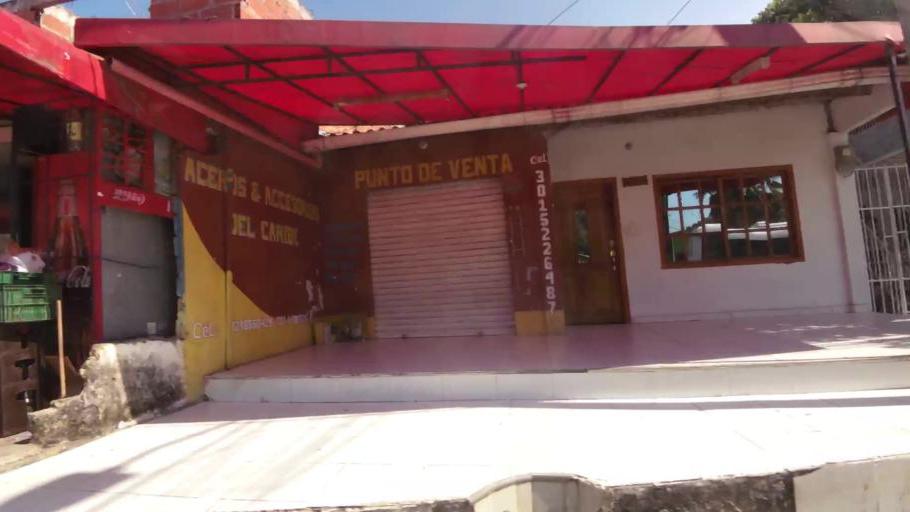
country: CO
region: Bolivar
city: Cartagena
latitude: 10.3807
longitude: -75.4701
